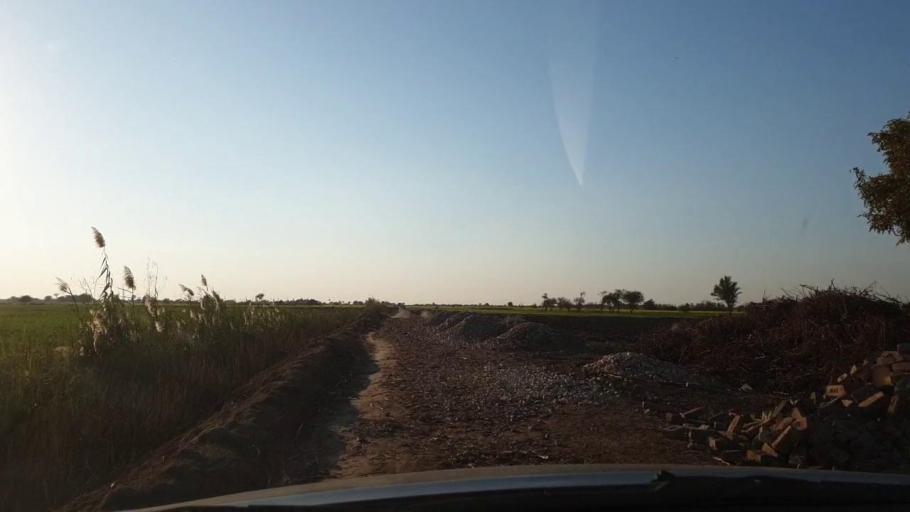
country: PK
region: Sindh
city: Tando Mittha Khan
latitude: 25.8327
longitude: 69.1610
